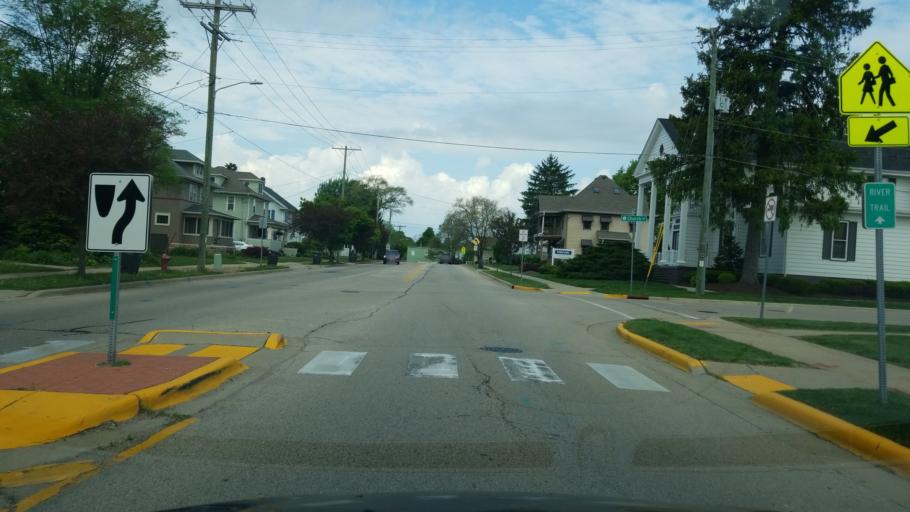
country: US
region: Wisconsin
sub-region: Dane County
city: Stoughton
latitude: 42.9186
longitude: -89.2109
